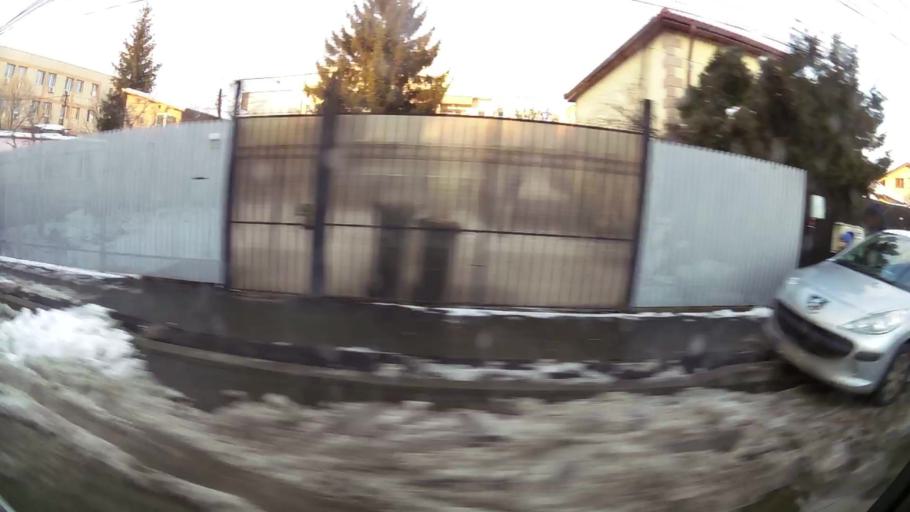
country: RO
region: Ilfov
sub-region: Comuna Popesti-Leordeni
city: Popesti-Leordeni
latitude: 44.3801
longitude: 26.1378
